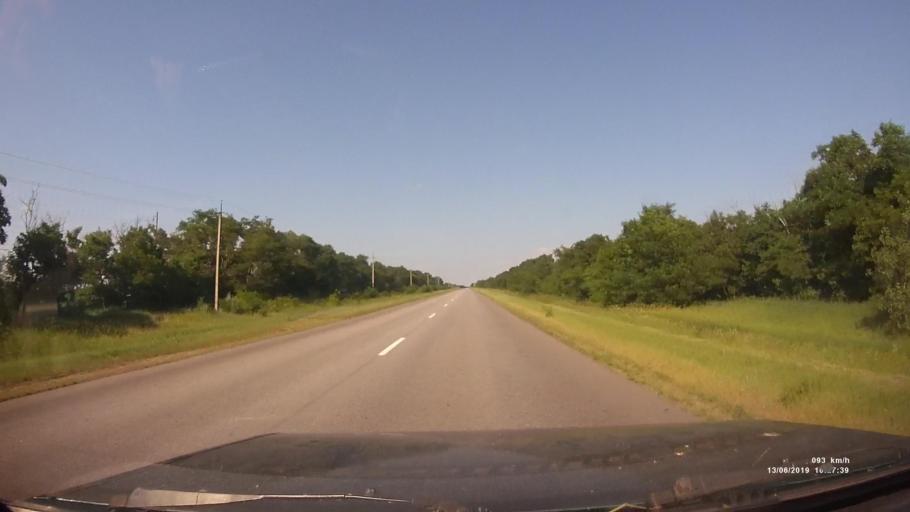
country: RU
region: Rostov
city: Kazanskaya
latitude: 49.8152
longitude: 41.1869
